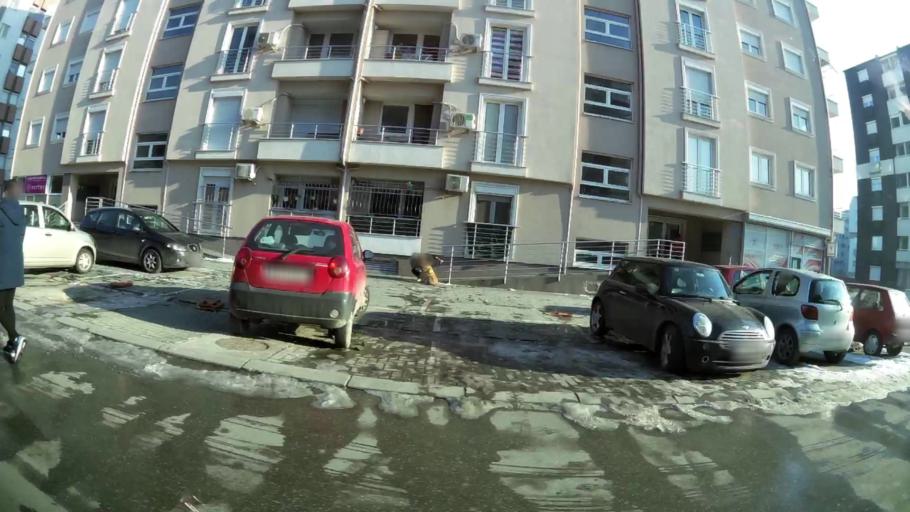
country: MK
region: Kisela Voda
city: Usje
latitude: 41.9826
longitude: 21.4572
